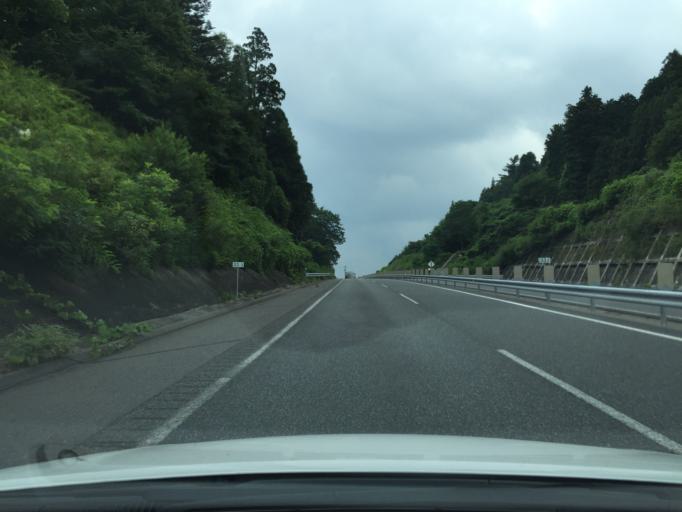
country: JP
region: Fukushima
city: Funehikimachi-funehiki
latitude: 37.2766
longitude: 140.6231
